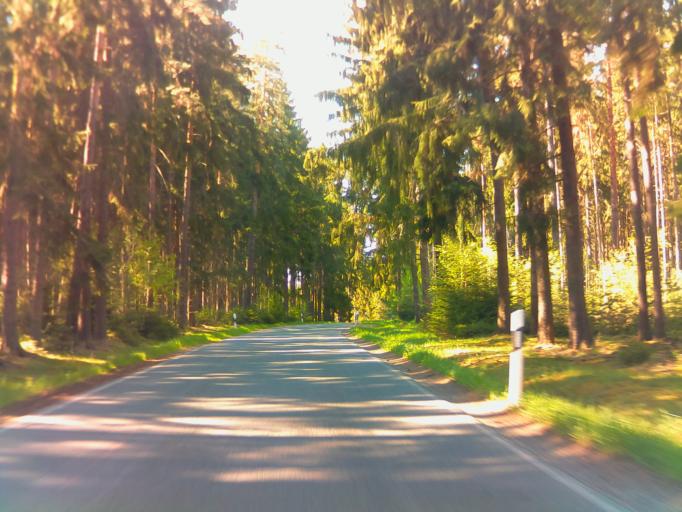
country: DE
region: Saxony
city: Pausa
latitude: 50.6032
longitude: 12.0378
